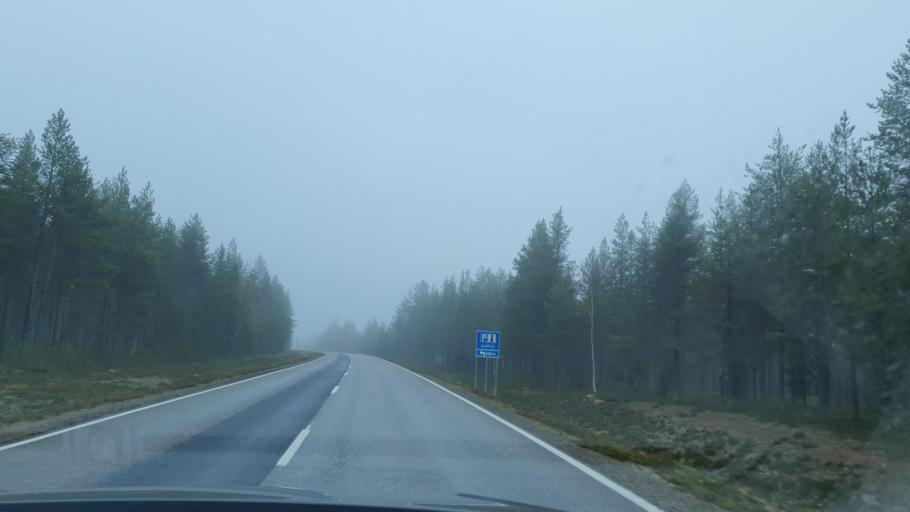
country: FI
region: Lapland
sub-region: Tunturi-Lappi
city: Kittilae
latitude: 67.3172
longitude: 24.9096
